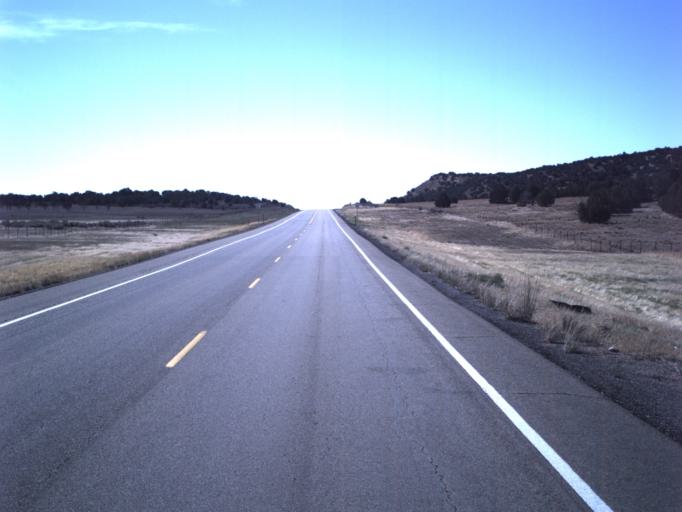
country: US
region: Utah
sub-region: Sanpete County
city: Gunnison
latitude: 39.3939
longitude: -111.9279
